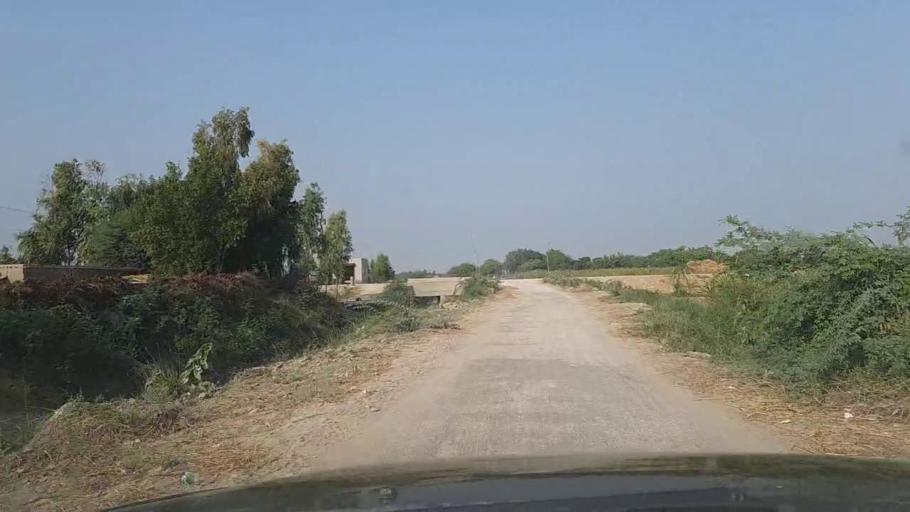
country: PK
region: Sindh
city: Mirpur Batoro
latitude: 24.7130
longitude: 68.2547
